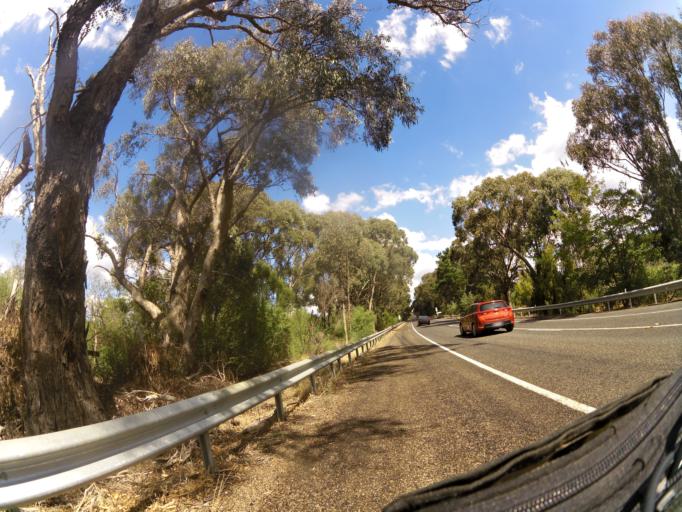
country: AU
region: Victoria
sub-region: Mansfield
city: Mansfield
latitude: -36.8303
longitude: 146.0086
